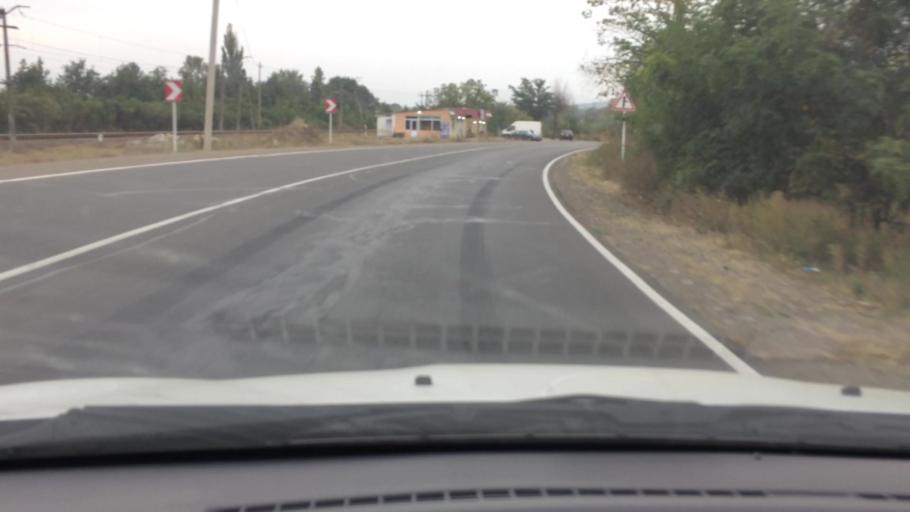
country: GE
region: Kvemo Kartli
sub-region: Marneuli
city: Marneuli
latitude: 41.4099
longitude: 44.8314
